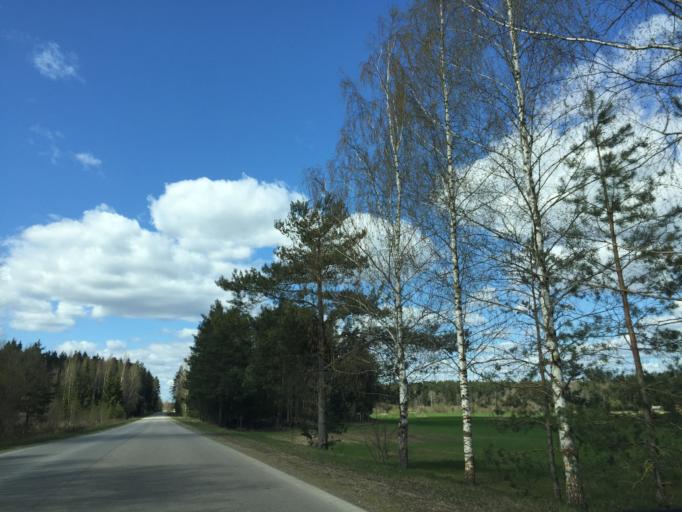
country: LV
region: Vilanu
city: Vilani
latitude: 56.5651
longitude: 27.0525
